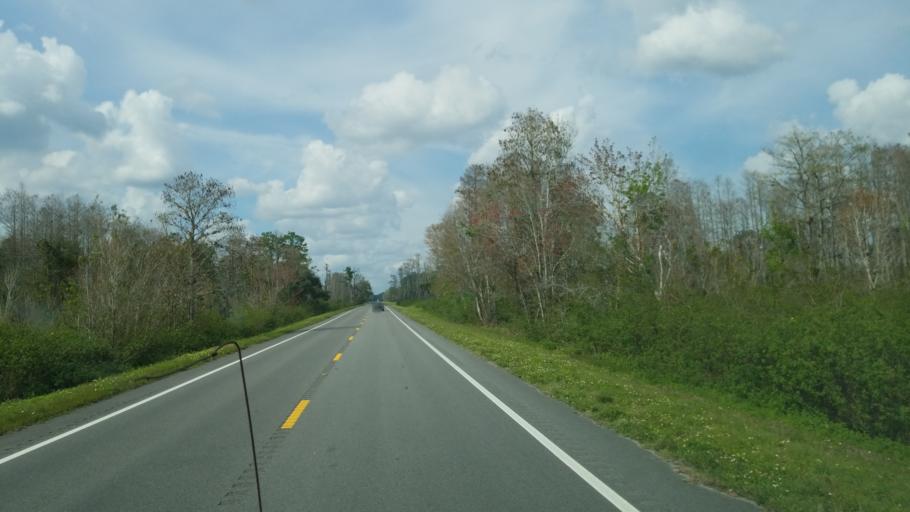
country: US
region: Florida
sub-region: Indian River County
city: Fellsmere
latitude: 27.7767
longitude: -80.9230
